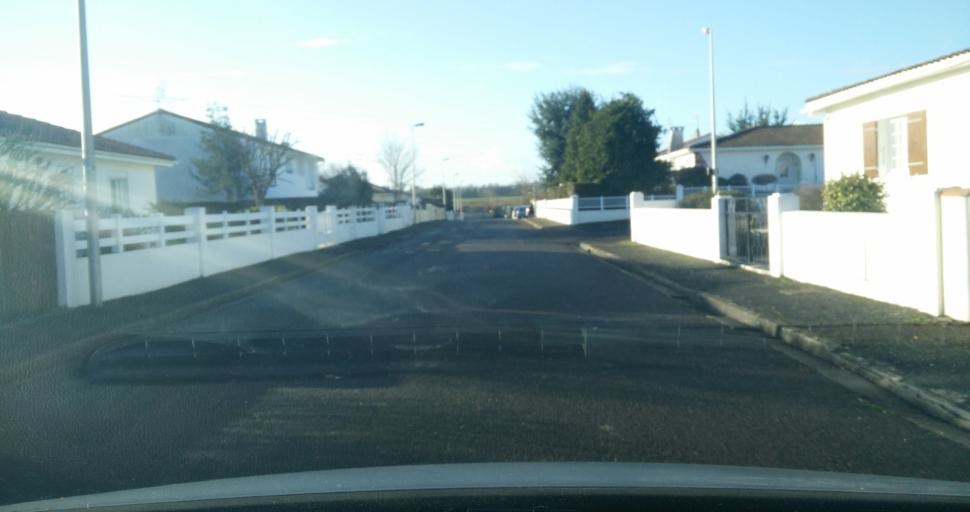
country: FR
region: Poitou-Charentes
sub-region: Departement de la Charente-Maritime
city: Saint-Xandre
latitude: 46.2011
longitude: -1.0968
